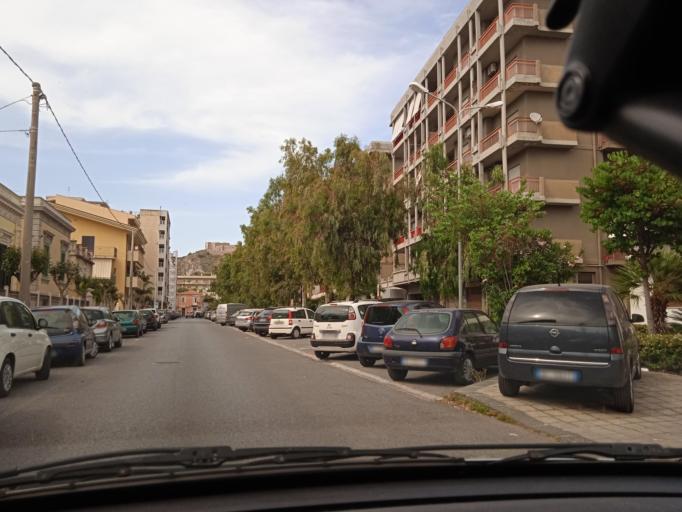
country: IT
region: Sicily
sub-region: Messina
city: Milazzo
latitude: 38.2239
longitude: 15.2394
